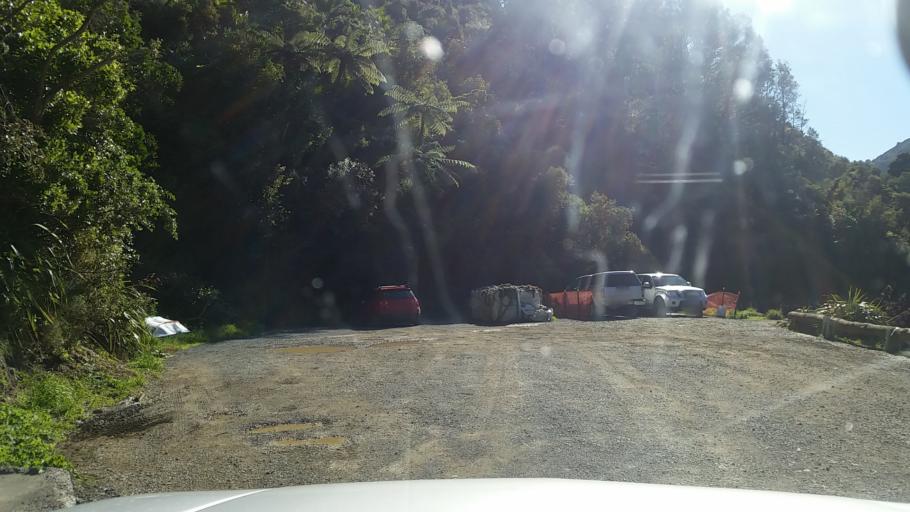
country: NZ
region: Marlborough
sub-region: Marlborough District
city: Picton
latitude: -41.1030
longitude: 173.6582
